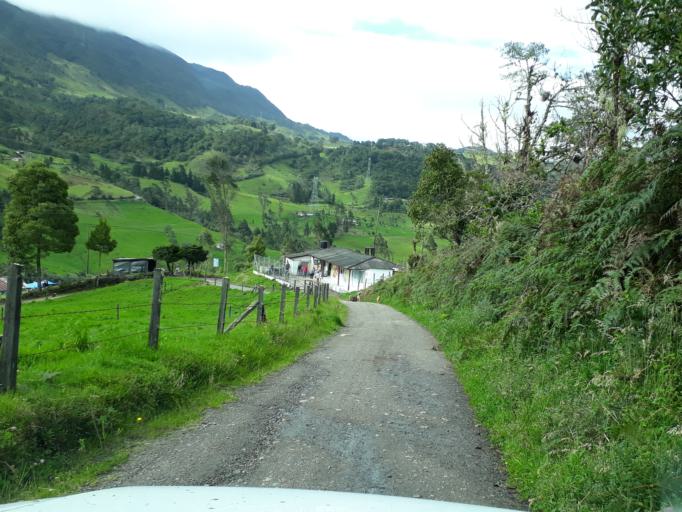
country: CO
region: Cundinamarca
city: Junin
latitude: 4.8218
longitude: -73.7693
